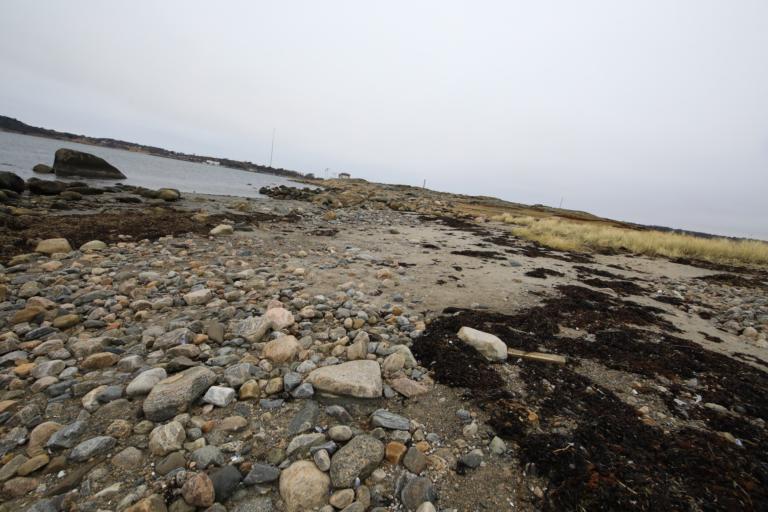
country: SE
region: Halland
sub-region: Kungsbacka Kommun
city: Frillesas
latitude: 57.2455
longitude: 12.1197
